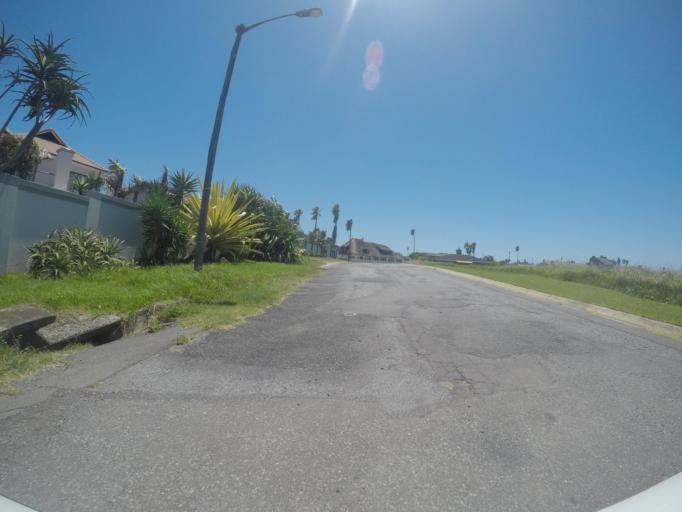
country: ZA
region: Eastern Cape
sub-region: Buffalo City Metropolitan Municipality
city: East London
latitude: -32.9534
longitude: 28.0111
